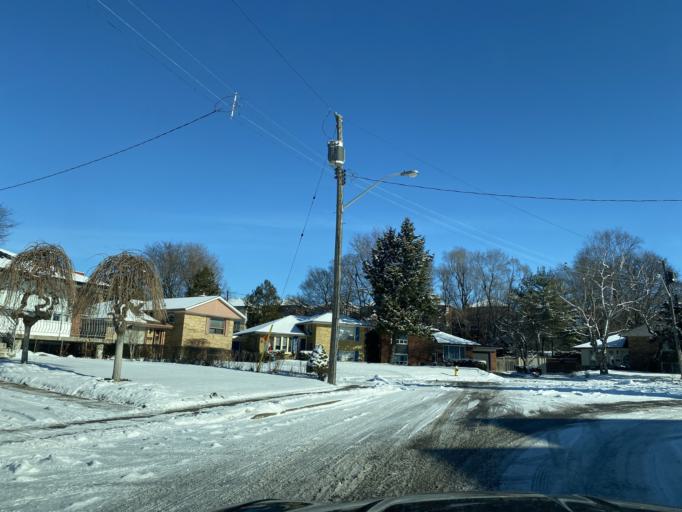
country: CA
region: Ontario
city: Scarborough
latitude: 43.7735
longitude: -79.3124
